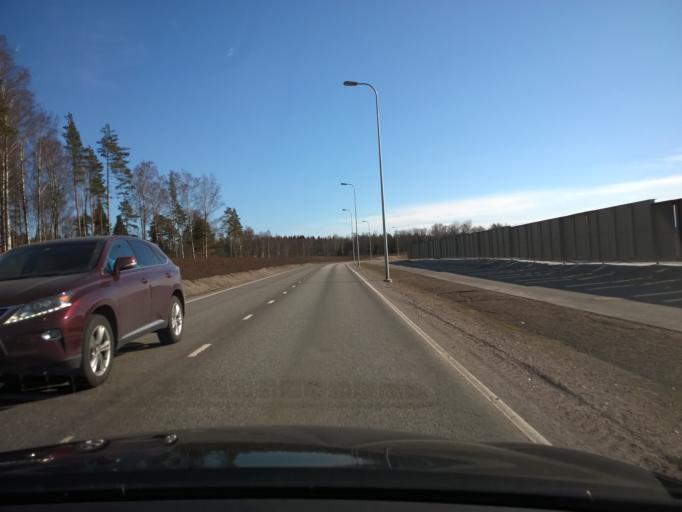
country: FI
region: Uusimaa
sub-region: Helsinki
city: Kilo
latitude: 60.1955
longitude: 24.7888
